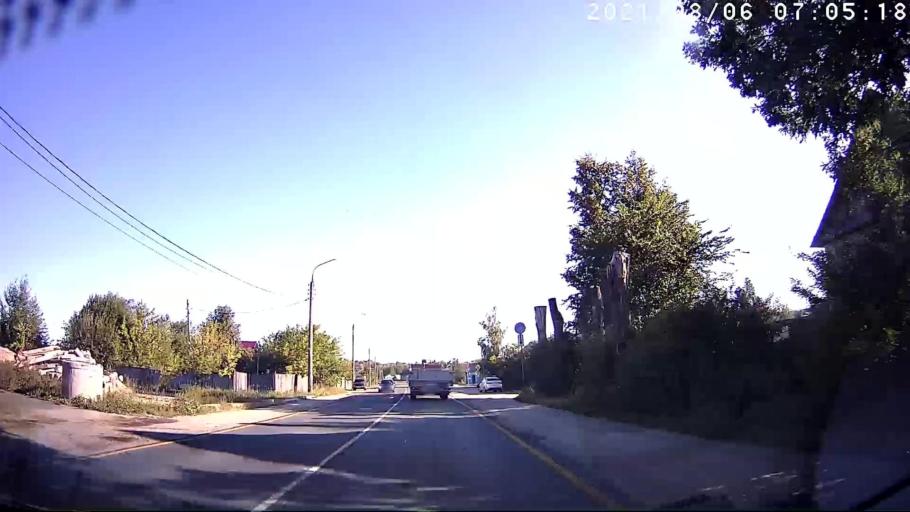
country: RU
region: Mariy-El
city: Yoshkar-Ola
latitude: 56.5526
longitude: 47.9864
